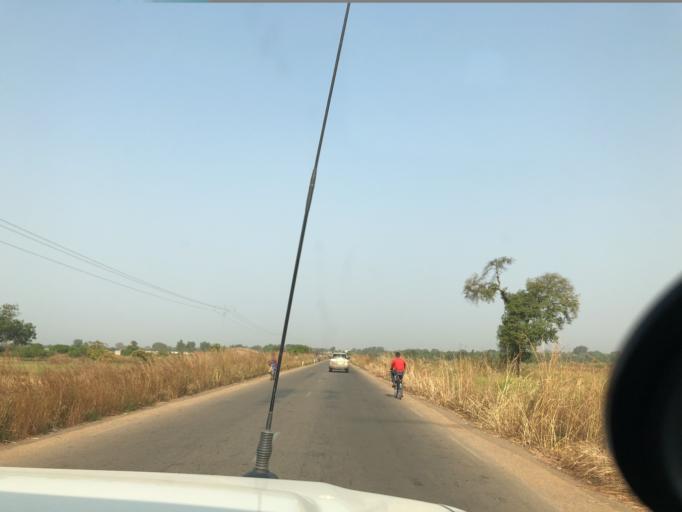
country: TD
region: Logone Occidental
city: Moundou
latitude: 8.5768
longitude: 16.0375
